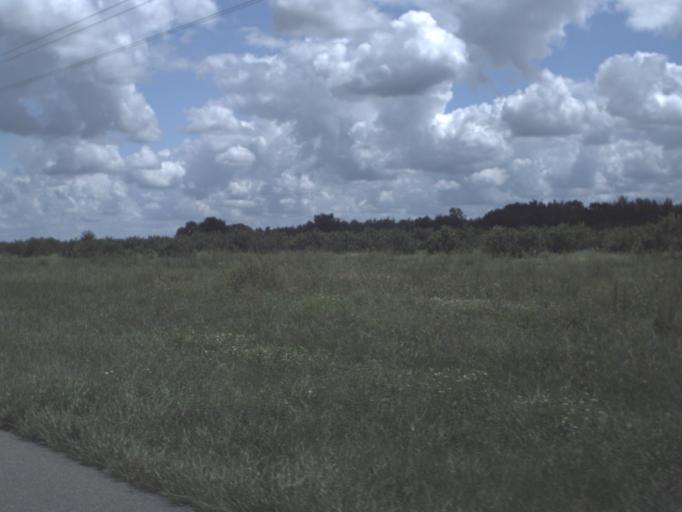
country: US
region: Florida
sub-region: Hillsborough County
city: Wimauma
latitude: 27.5814
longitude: -82.1869
